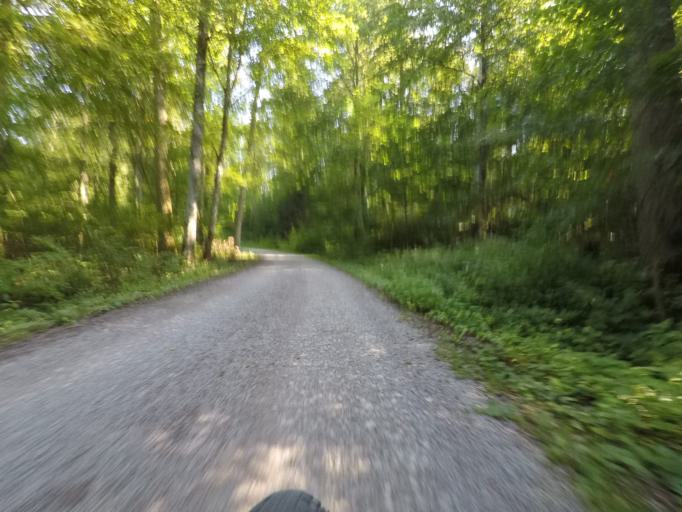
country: DE
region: Baden-Wuerttemberg
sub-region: Regierungsbezirk Stuttgart
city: Hildrizhausen
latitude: 48.6503
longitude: 8.9703
